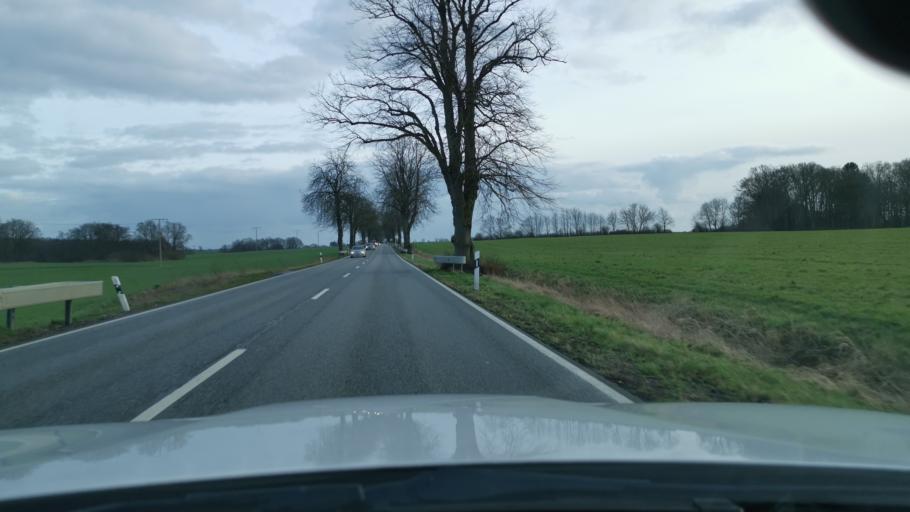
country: DE
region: Mecklenburg-Vorpommern
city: Dummerstorf
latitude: 53.9880
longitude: 12.2722
